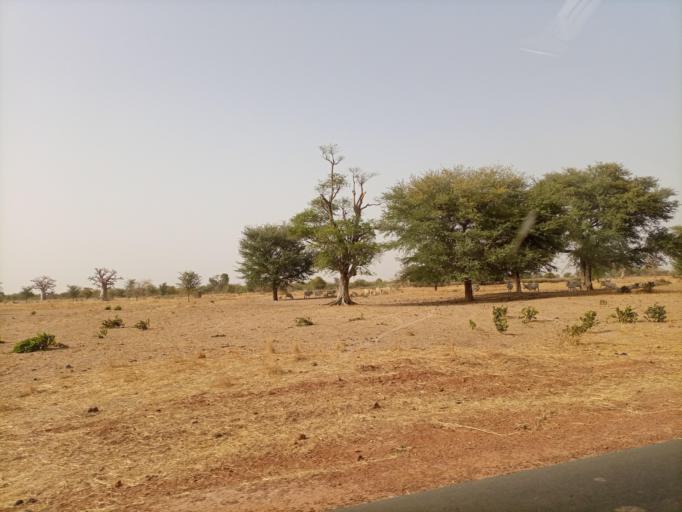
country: SN
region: Fatick
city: Foundiougne
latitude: 14.1282
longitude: -16.4109
